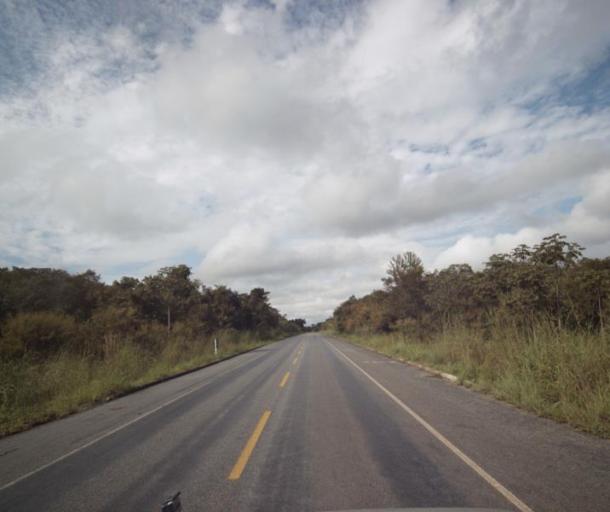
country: BR
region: Goias
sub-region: Pirenopolis
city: Pirenopolis
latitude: -15.5243
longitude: -48.6247
